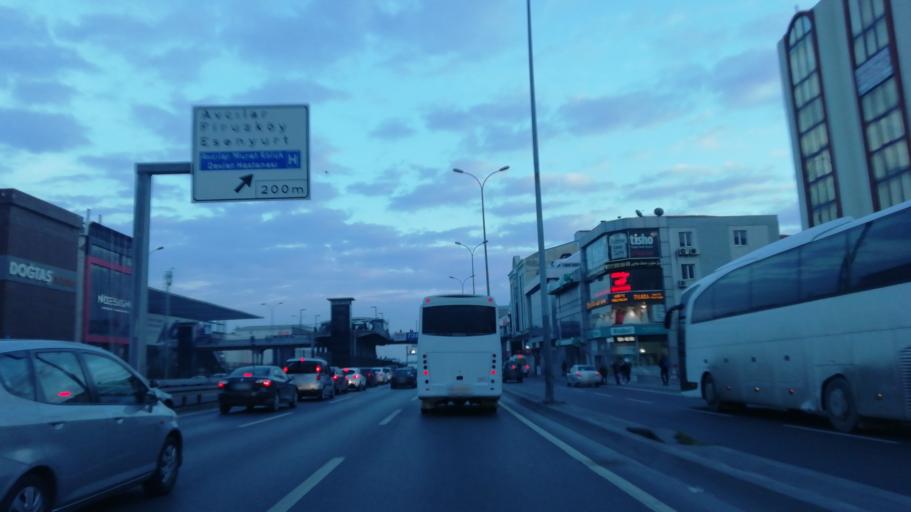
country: TR
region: Istanbul
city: Yakuplu
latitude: 40.9914
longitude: 28.7123
